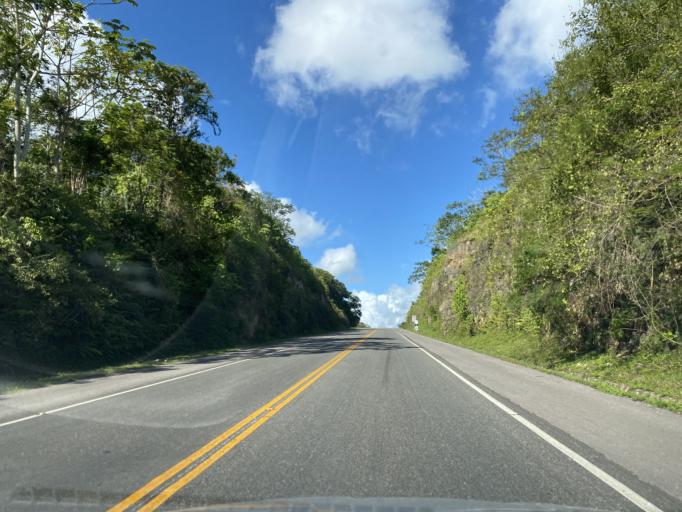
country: DO
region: Monte Plata
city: Majagual
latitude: 19.0357
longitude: -69.8272
